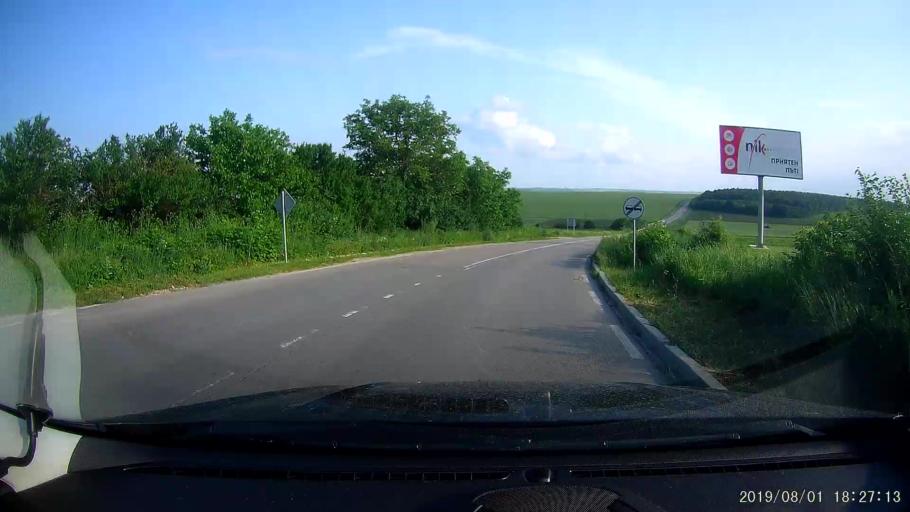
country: BG
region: Shumen
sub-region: Obshtina Venets
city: Venets
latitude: 43.5907
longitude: 26.9834
